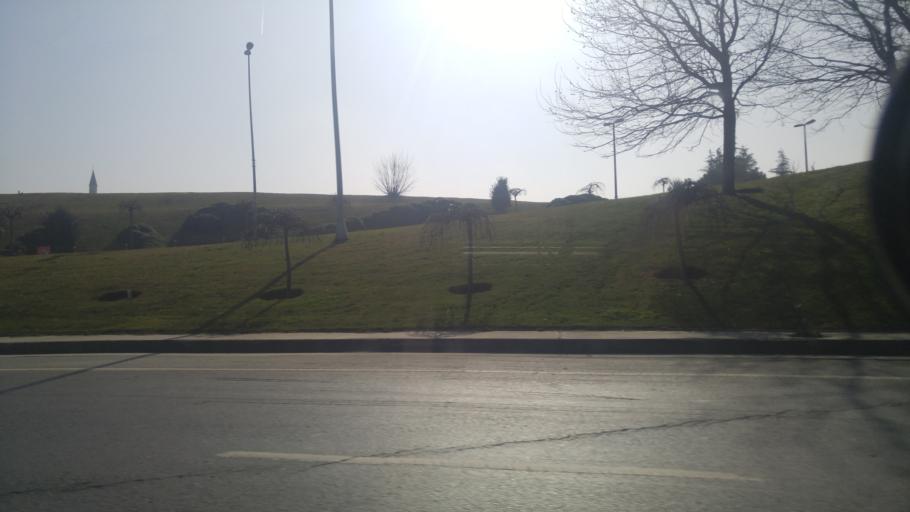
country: TR
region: Istanbul
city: Bahcelievler
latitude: 40.9824
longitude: 28.8216
